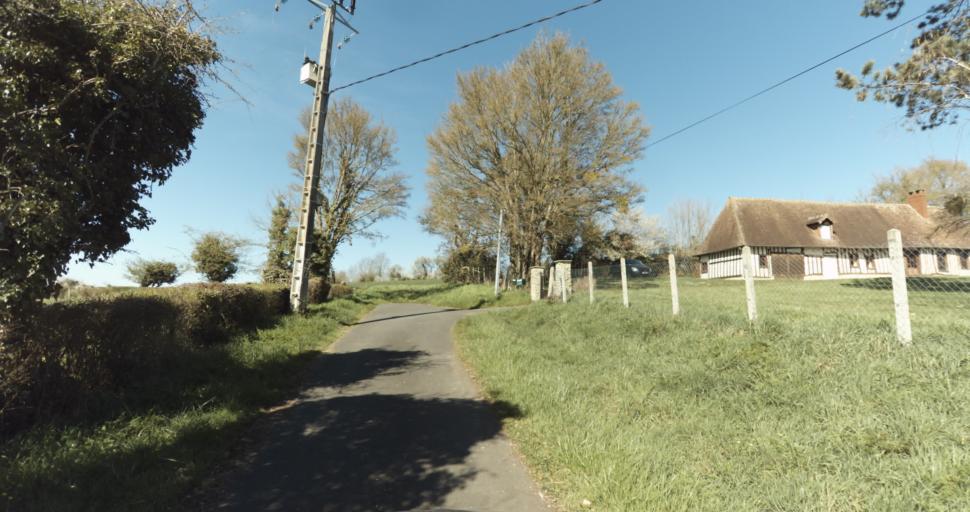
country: FR
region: Lower Normandy
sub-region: Departement du Calvados
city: Saint-Pierre-sur-Dives
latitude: 49.0516
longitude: -0.0159
